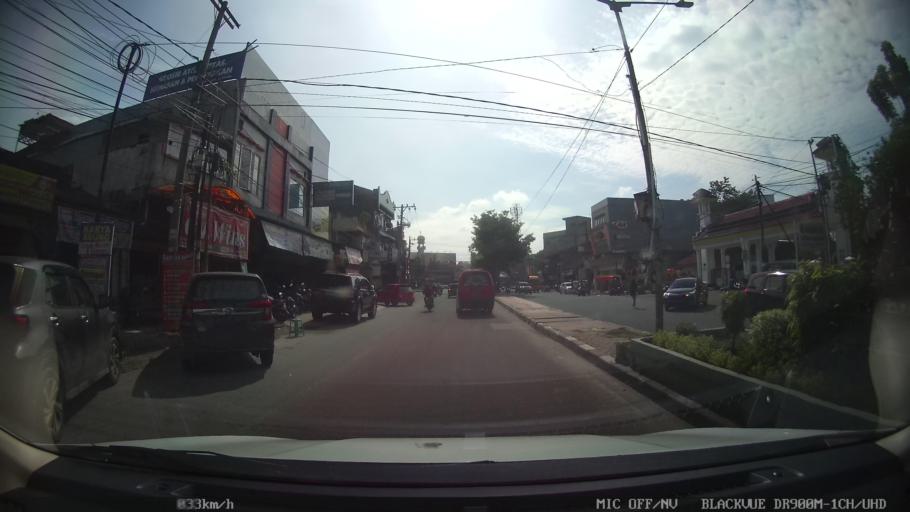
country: ID
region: North Sumatra
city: Medan
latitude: 3.5673
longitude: 98.6590
